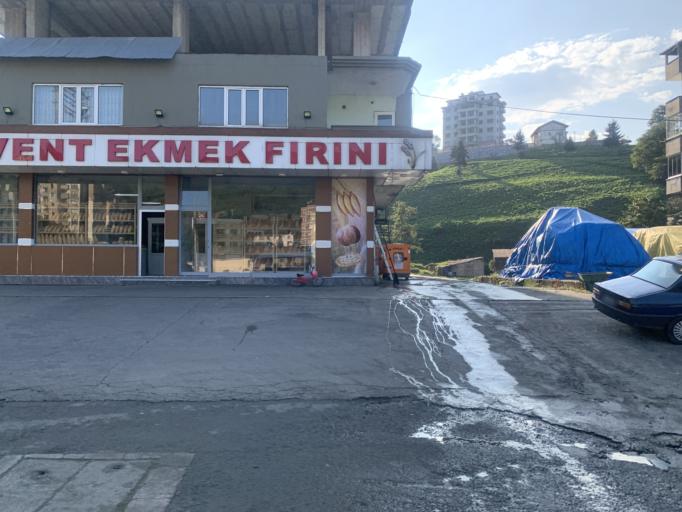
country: TR
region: Trabzon
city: Of
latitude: 40.9380
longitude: 40.2728
